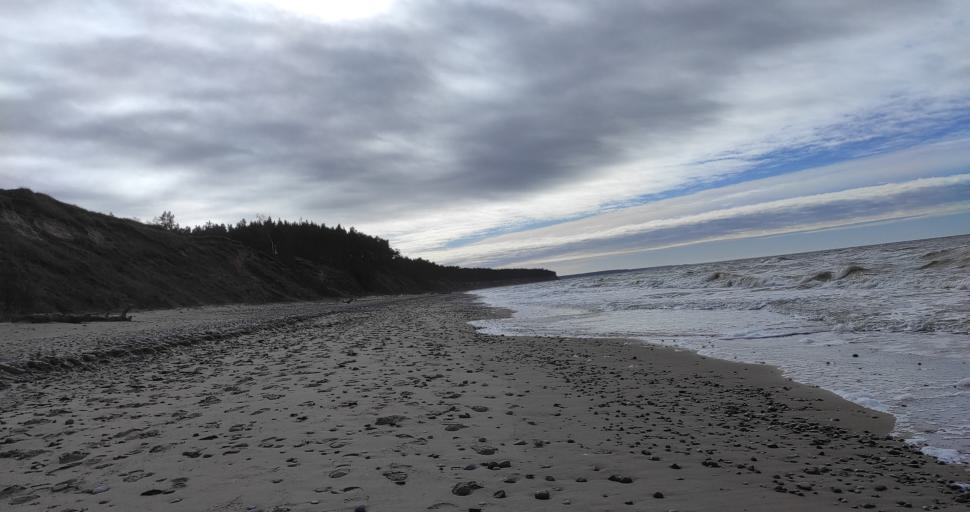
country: LV
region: Alsunga
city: Alsunga
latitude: 57.0347
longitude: 21.4005
